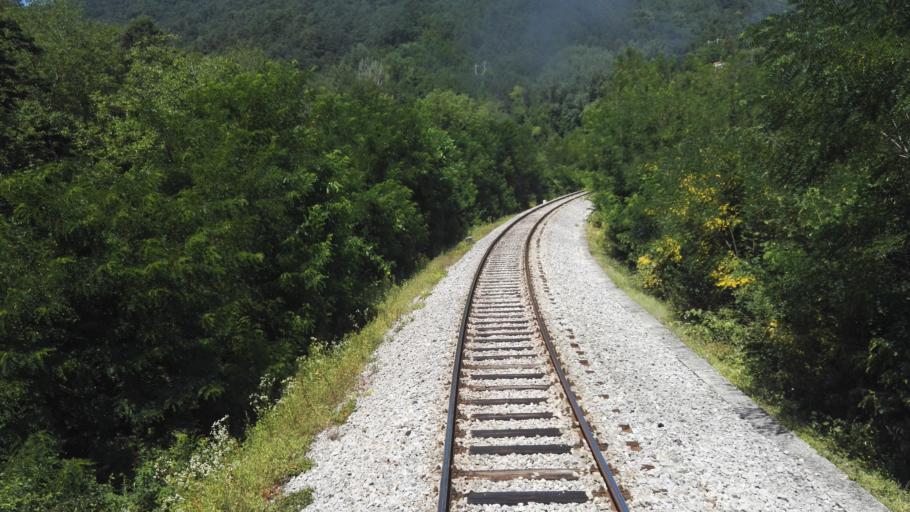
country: SI
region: Kanal
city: Deskle
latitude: 46.0287
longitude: 13.5956
